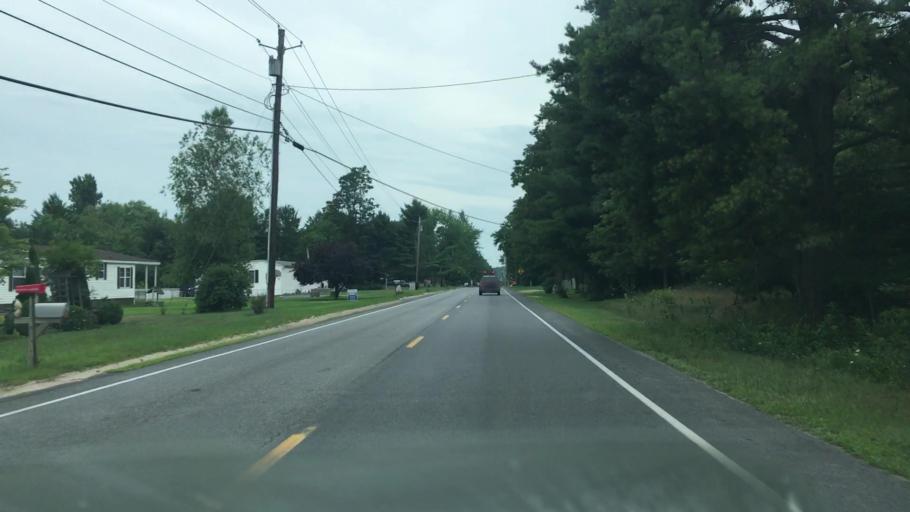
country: US
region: New York
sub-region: Clinton County
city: Plattsburgh West
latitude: 44.6559
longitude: -73.5109
